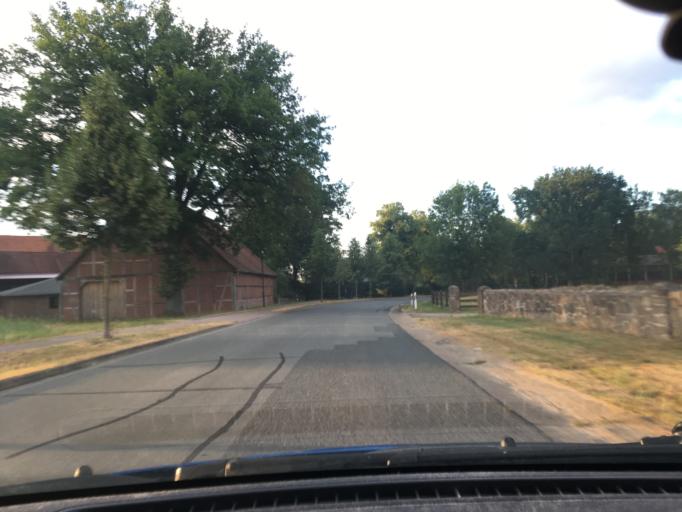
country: DE
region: Lower Saxony
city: Eyendorf
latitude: 53.1943
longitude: 10.1915
